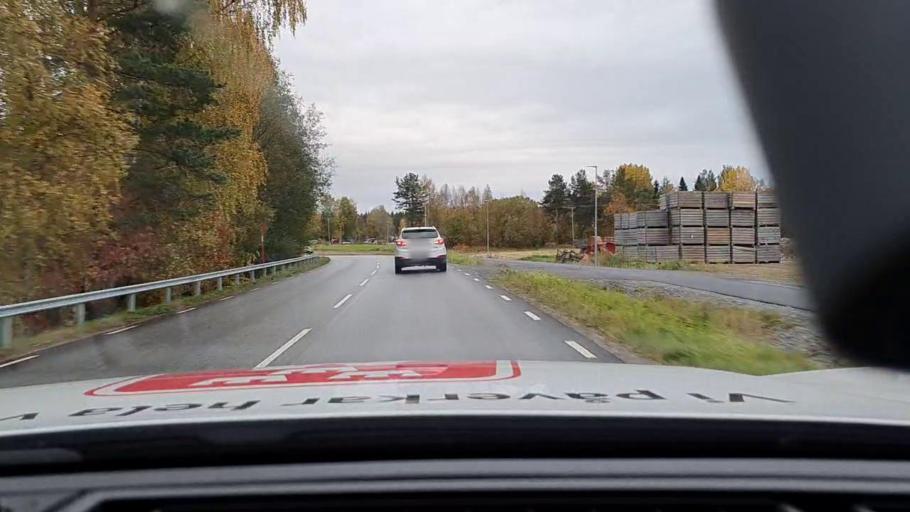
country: SE
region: Norrbotten
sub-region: Bodens Kommun
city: Saevast
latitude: 65.7693
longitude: 21.7066
